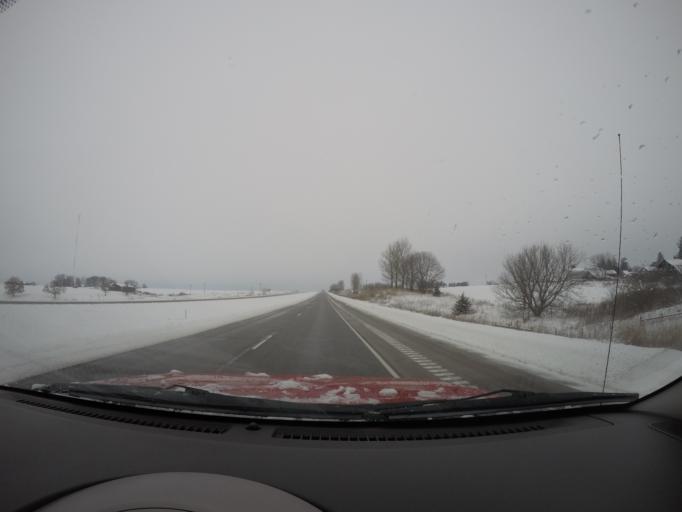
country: US
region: Minnesota
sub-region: Winona County
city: Goodview
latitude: 43.9453
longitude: -91.7181
